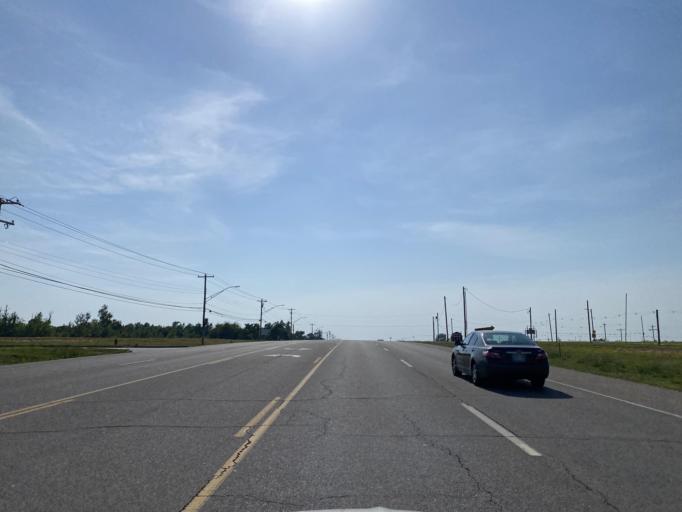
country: US
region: Oklahoma
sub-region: Oklahoma County
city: Nicoma Park
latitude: 35.4931
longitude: -97.3425
